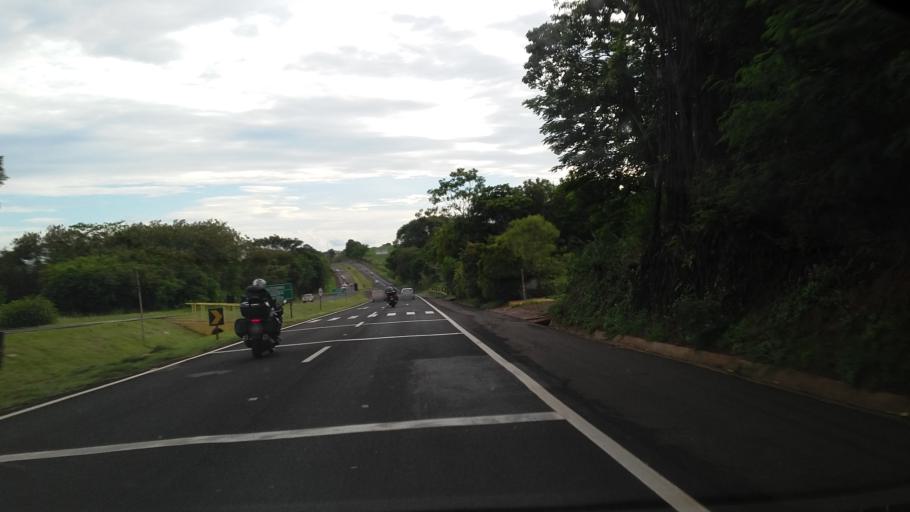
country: BR
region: Parana
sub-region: Paicandu
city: Paicandu
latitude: -23.5098
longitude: -52.0236
